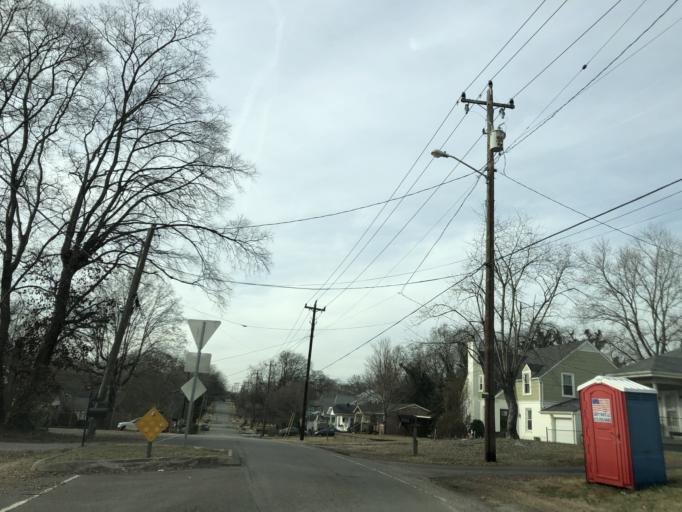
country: US
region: Tennessee
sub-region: Davidson County
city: Nashville
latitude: 36.2079
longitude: -86.7282
